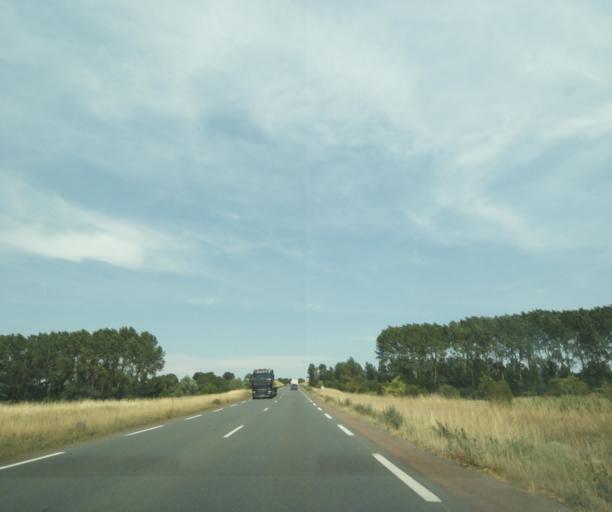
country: FR
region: Poitou-Charentes
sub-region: Departement de la Vienne
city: Cenon-sur-Vienne
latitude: 46.7887
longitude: 0.5512
